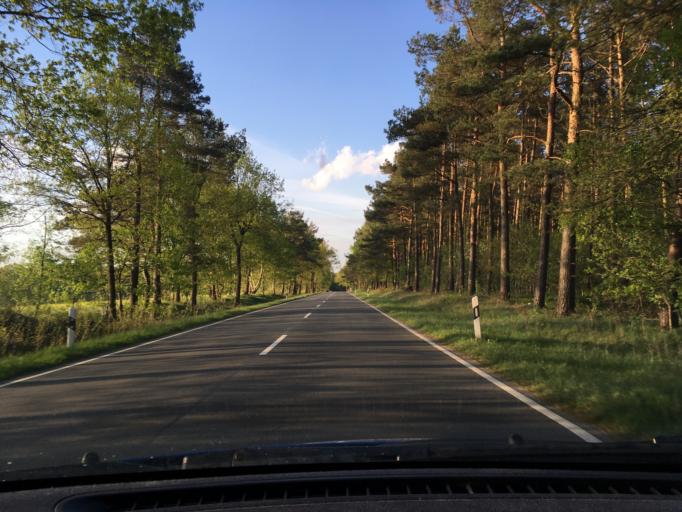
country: DE
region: Lower Saxony
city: Wietzendorf
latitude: 52.8760
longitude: 9.9824
